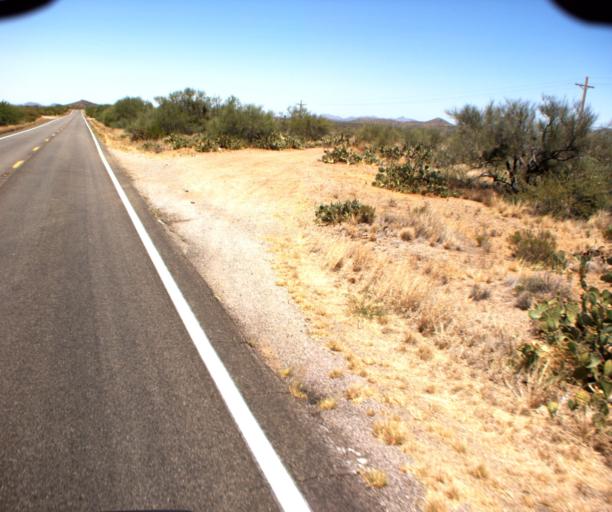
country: US
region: Arizona
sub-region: Pima County
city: Catalina
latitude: 32.6394
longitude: -111.0130
